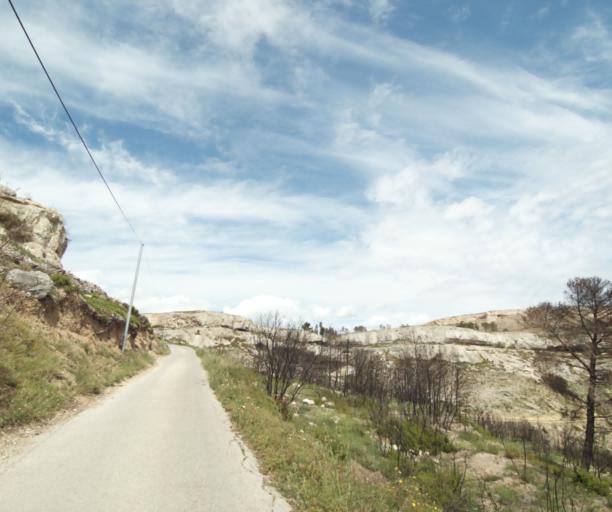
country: FR
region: Provence-Alpes-Cote d'Azur
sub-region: Departement des Bouches-du-Rhone
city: Rognac
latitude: 43.4846
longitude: 5.2495
